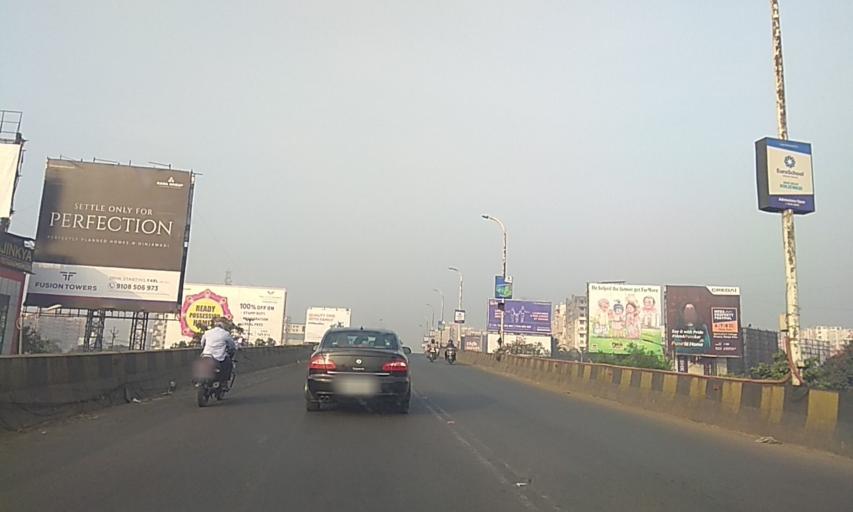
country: IN
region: Maharashtra
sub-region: Pune Division
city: Pimpri
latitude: 18.5921
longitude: 73.7584
